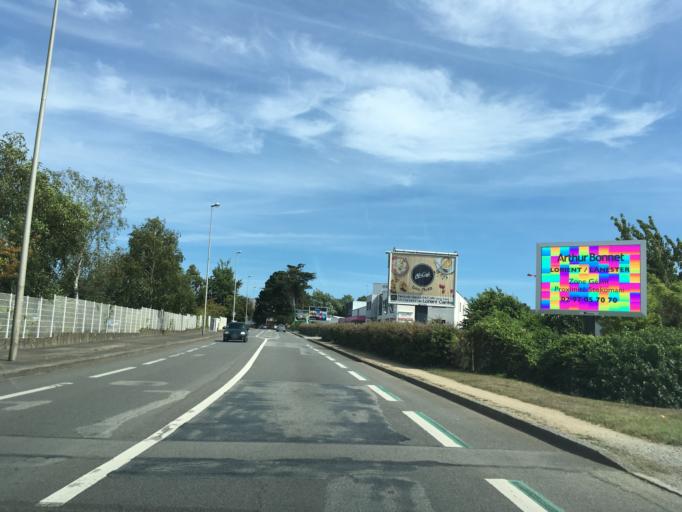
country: FR
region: Brittany
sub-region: Departement du Morbihan
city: Lorient
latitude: 47.7531
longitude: -3.3827
